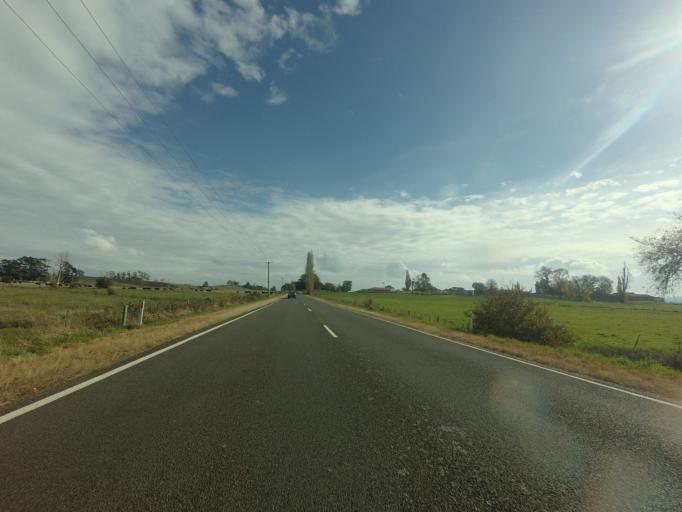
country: AU
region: Tasmania
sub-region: Meander Valley
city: Deloraine
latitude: -41.5249
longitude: 146.7073
